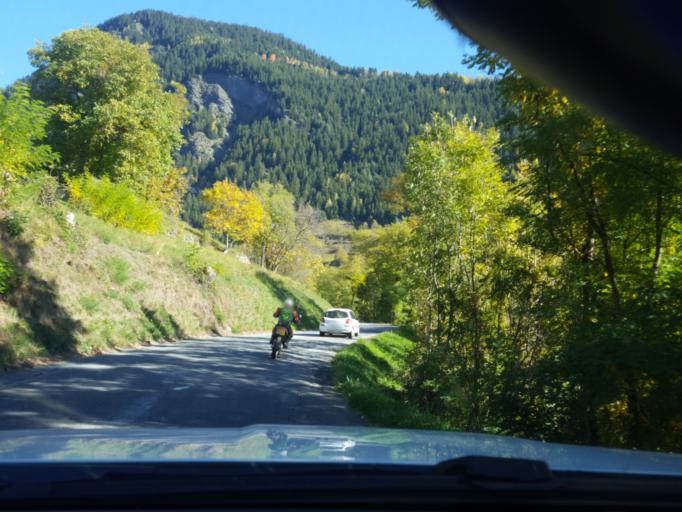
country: FR
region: Rhone-Alpes
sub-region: Departement de la Savoie
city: Seez
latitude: 45.6279
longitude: 6.7837
